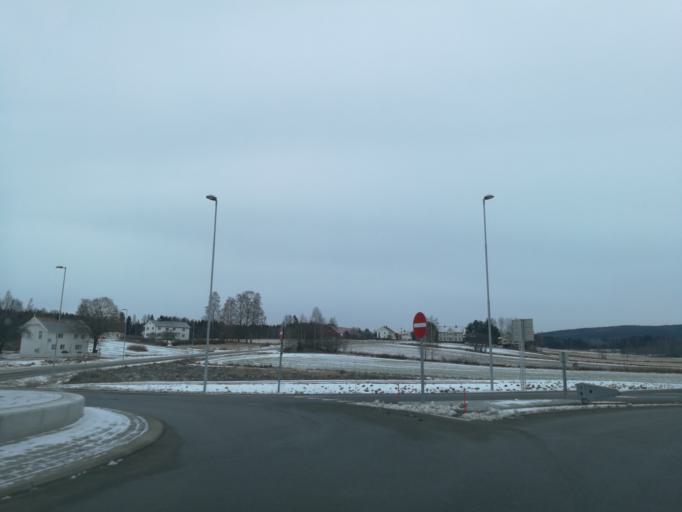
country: NO
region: Hedmark
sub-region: Kongsvinger
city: Spetalen
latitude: 60.2353
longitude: 11.8212
